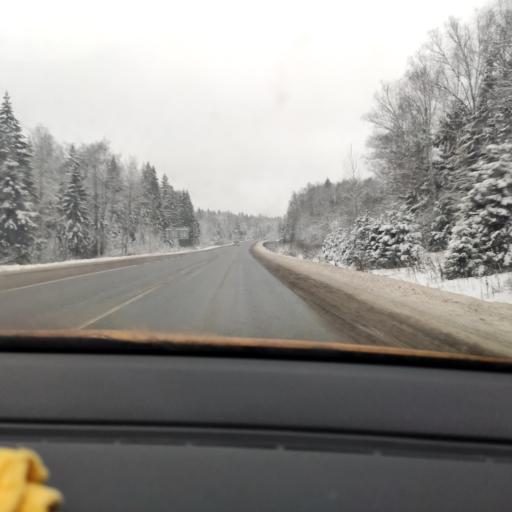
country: RU
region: Moskovskaya
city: Yershovo
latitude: 55.8014
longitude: 36.9439
